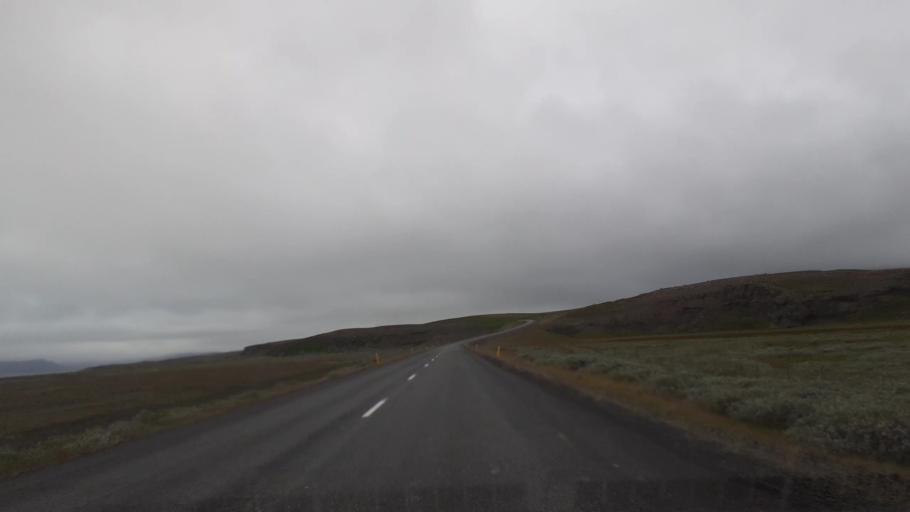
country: IS
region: Northeast
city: Husavik
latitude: 66.2035
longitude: -16.4720
